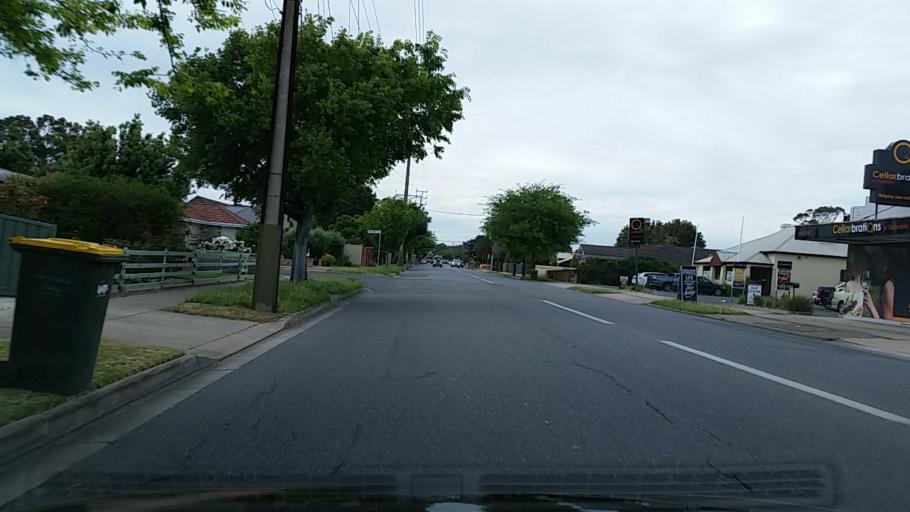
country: AU
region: South Australia
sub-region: City of West Torrens
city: Thebarton
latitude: -34.9216
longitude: 138.5487
